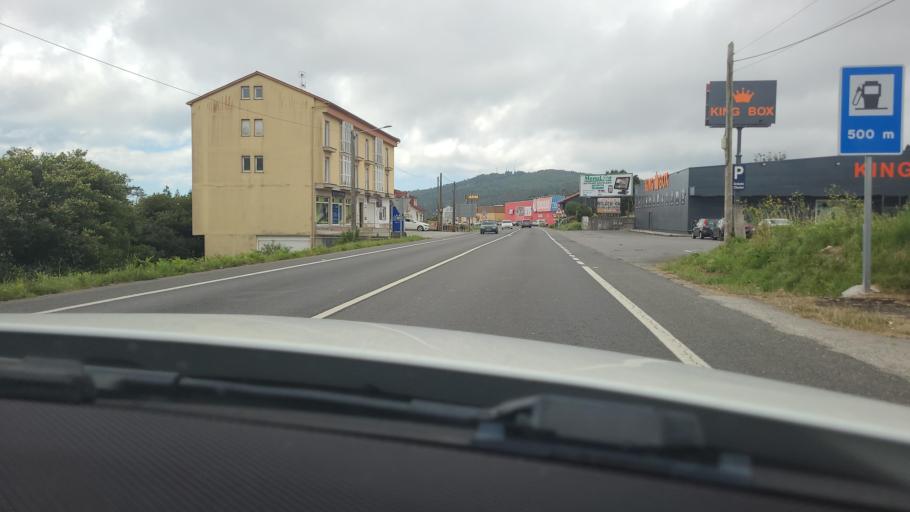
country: ES
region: Galicia
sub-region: Provincia da Coruna
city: Cee
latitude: 42.9710
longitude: -9.1912
